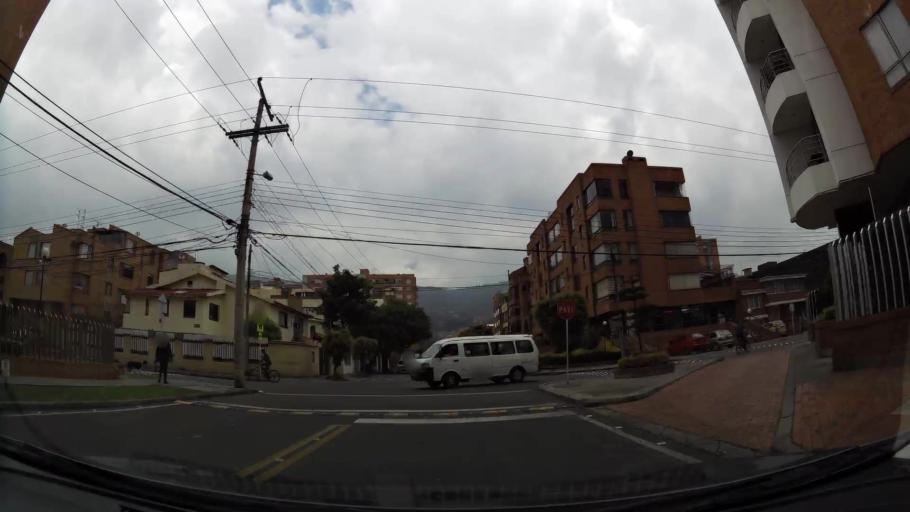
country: CO
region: Bogota D.C.
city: Barrio San Luis
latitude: 4.7222
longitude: -74.0343
